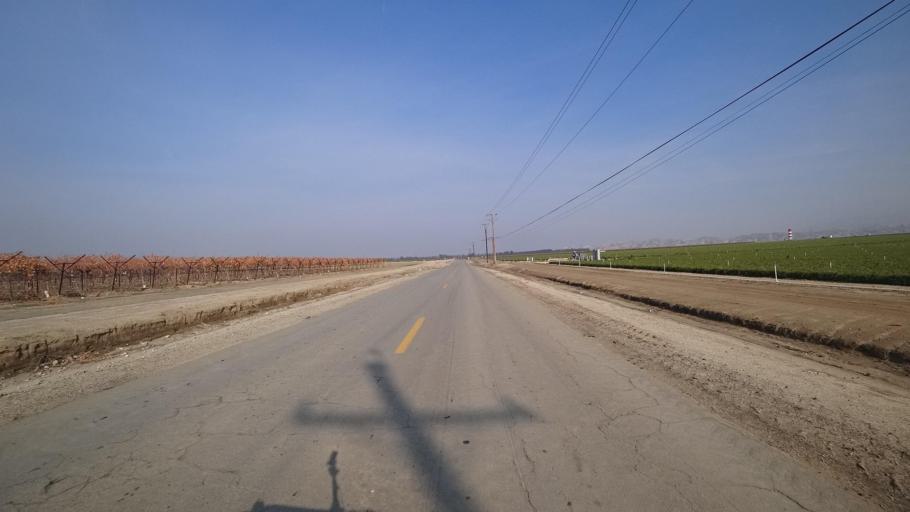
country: US
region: California
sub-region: Kern County
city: Arvin
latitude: 35.0882
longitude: -118.8465
